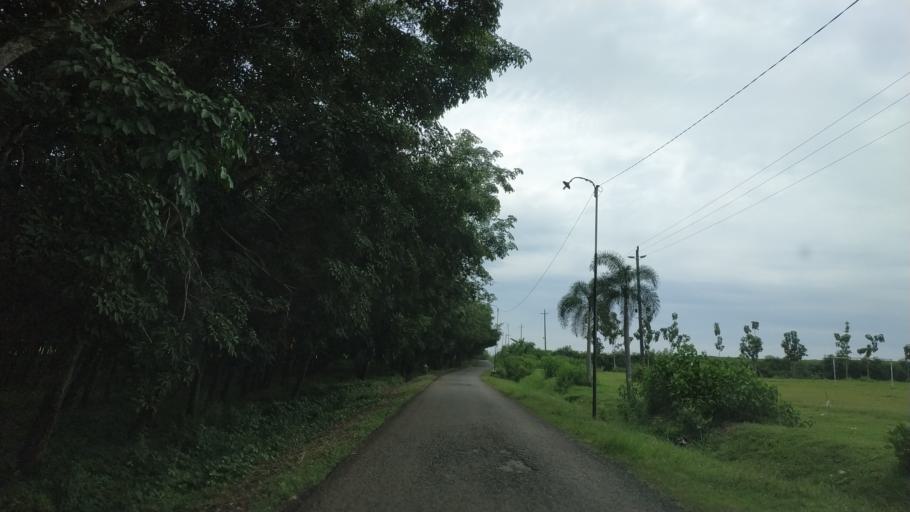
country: ID
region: Central Java
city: Krajan Tegalombo
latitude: -6.4293
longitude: 110.9836
